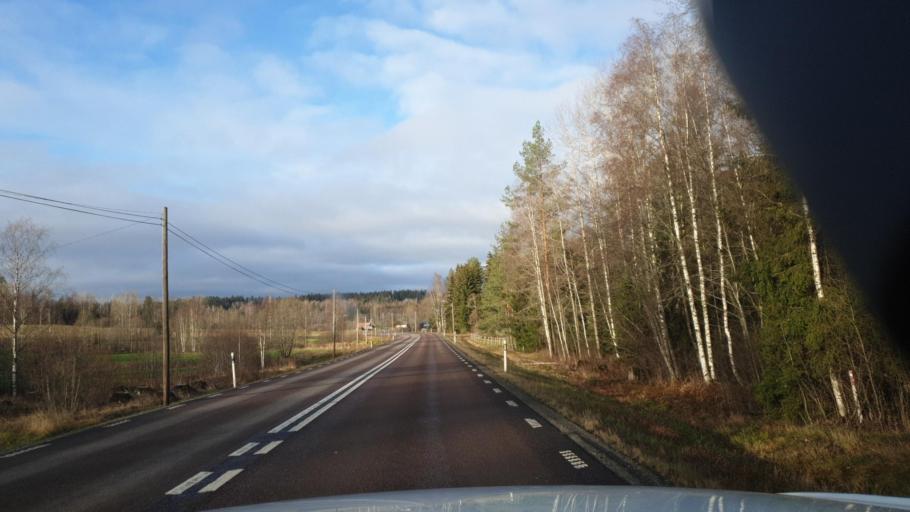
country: SE
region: Vaermland
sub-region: Sunne Kommun
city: Sunne
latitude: 59.6657
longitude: 12.9176
